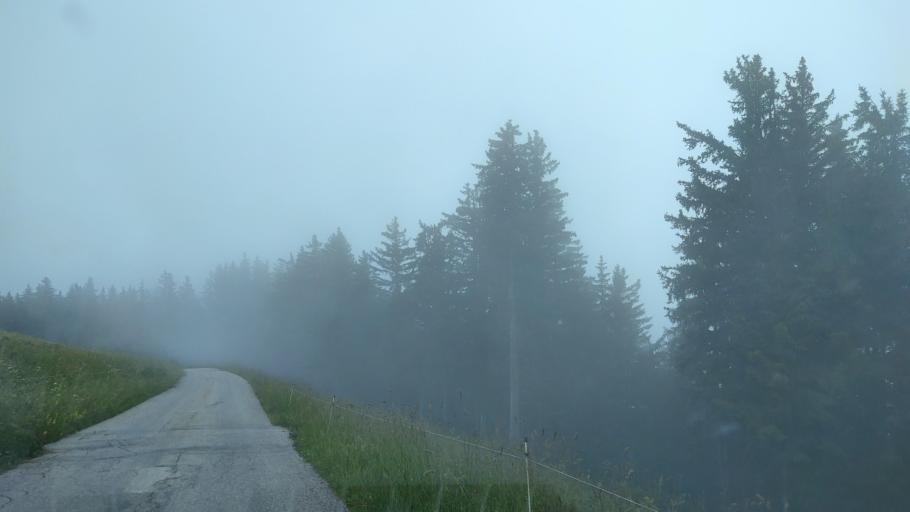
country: FR
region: Rhone-Alpes
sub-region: Departement de la Savoie
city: Beaufort
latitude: 45.7473
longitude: 6.5242
